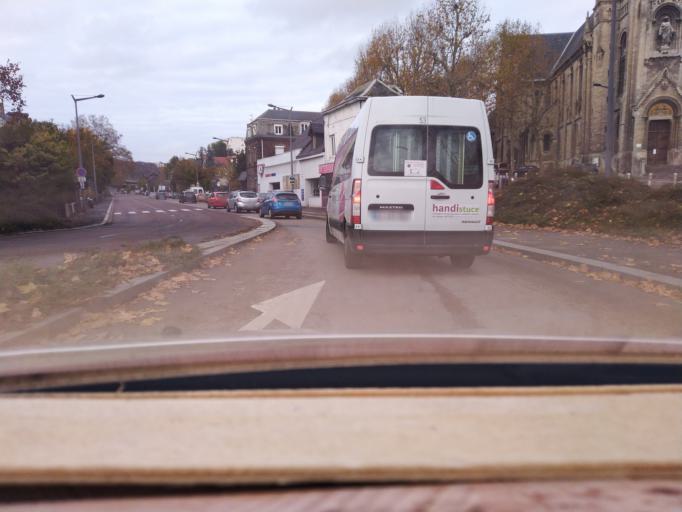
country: FR
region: Haute-Normandie
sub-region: Departement de la Seine-Maritime
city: Deville-les-Rouen
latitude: 49.4496
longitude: 1.0633
